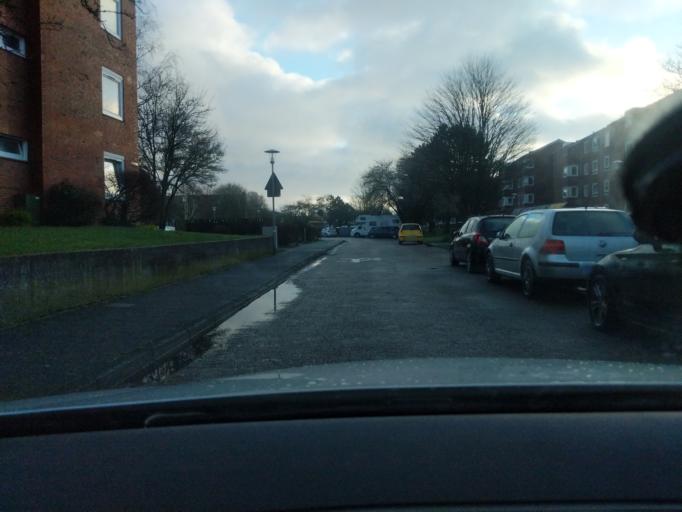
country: DE
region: Lower Saxony
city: Cuxhaven
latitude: 53.8539
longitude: 8.6836
